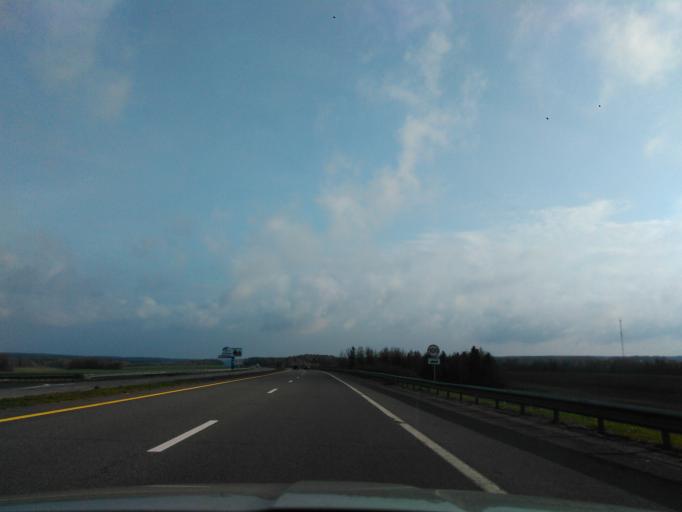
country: BY
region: Minsk
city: Lahoysk
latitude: 54.1560
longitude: 27.8114
